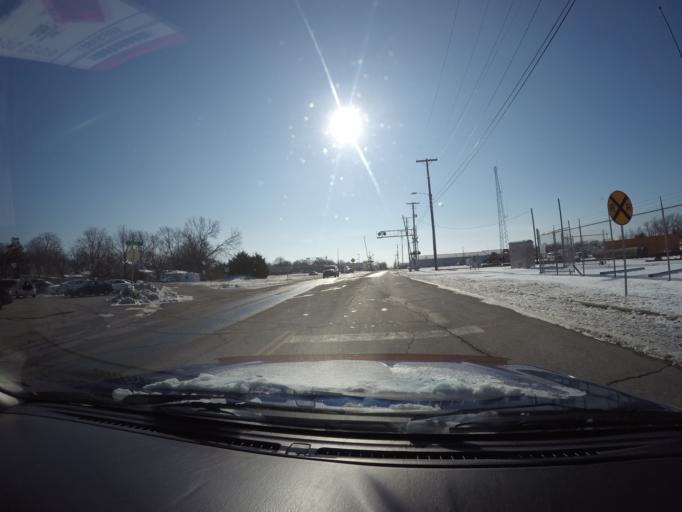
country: US
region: Kansas
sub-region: Johnson County
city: Olathe
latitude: 38.8758
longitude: -94.8207
